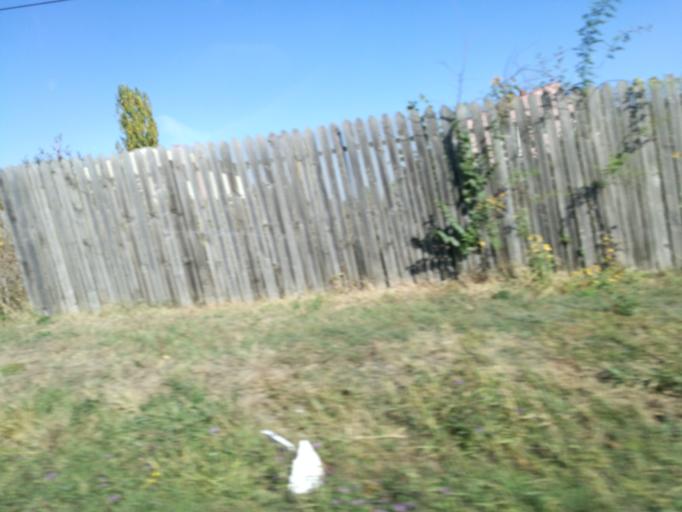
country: RO
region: Ilfov
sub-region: Comuna Dragomiresti-Vale
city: Dragomiresti-Vale
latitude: 44.4688
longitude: 25.9213
